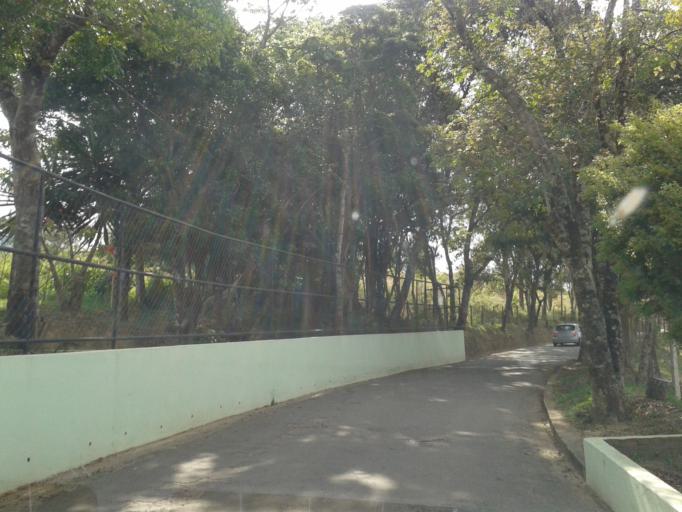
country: BR
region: Minas Gerais
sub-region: Caete
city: Caete
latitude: -19.7693
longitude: -43.6316
